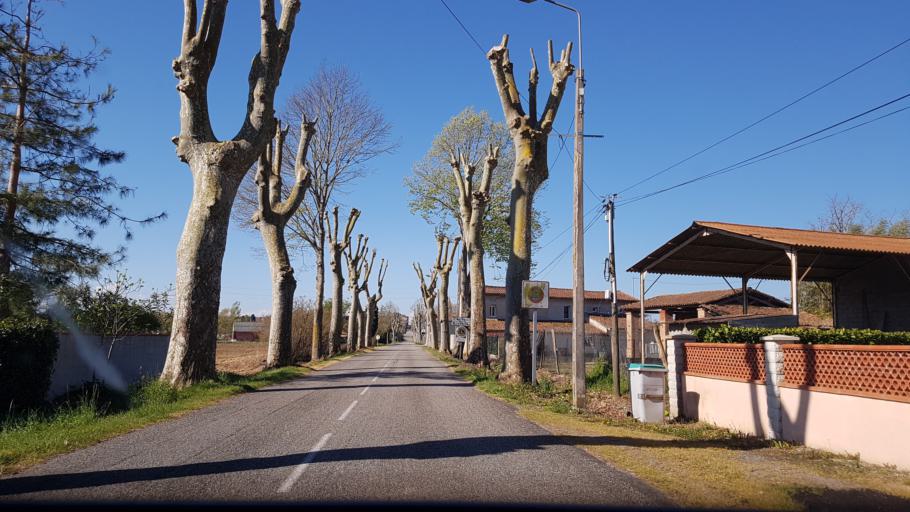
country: FR
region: Midi-Pyrenees
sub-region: Departement de l'Ariege
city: Mazeres
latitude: 43.2573
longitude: 1.6854
